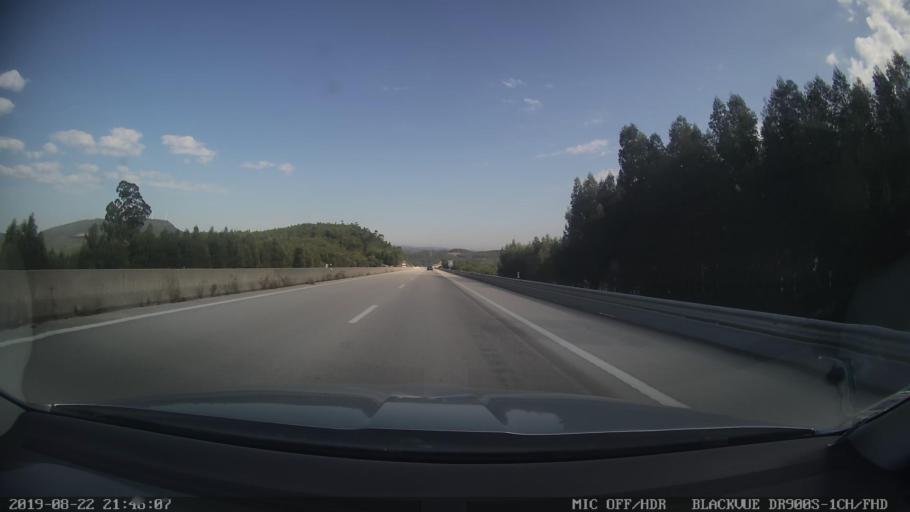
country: PT
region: Coimbra
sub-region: Penela
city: Penela
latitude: 39.9815
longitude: -8.3585
